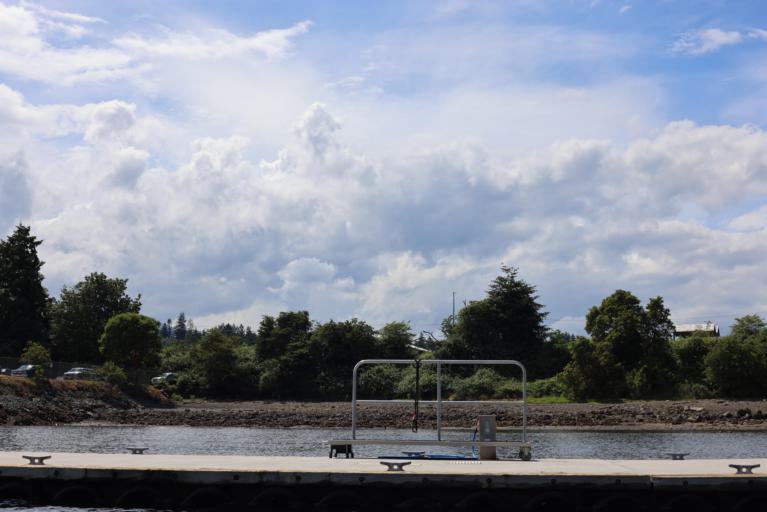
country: CA
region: British Columbia
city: Nanaimo
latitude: 49.1924
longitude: -123.9479
